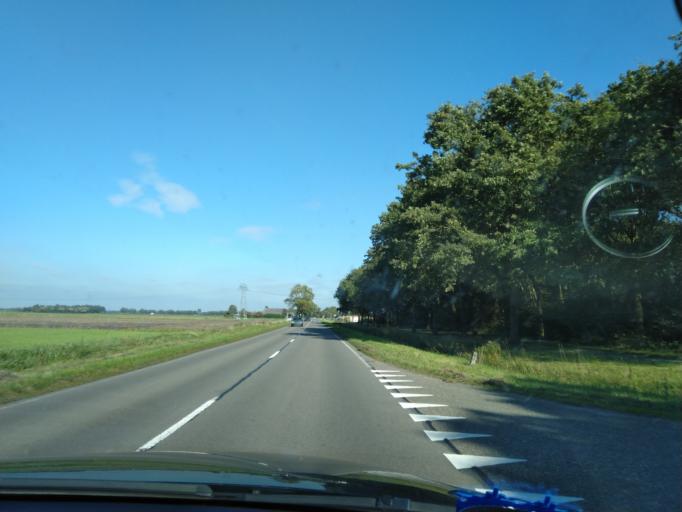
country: NL
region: Drenthe
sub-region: Gemeente Aa en Hunze
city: Anloo
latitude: 53.0578
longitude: 6.7397
